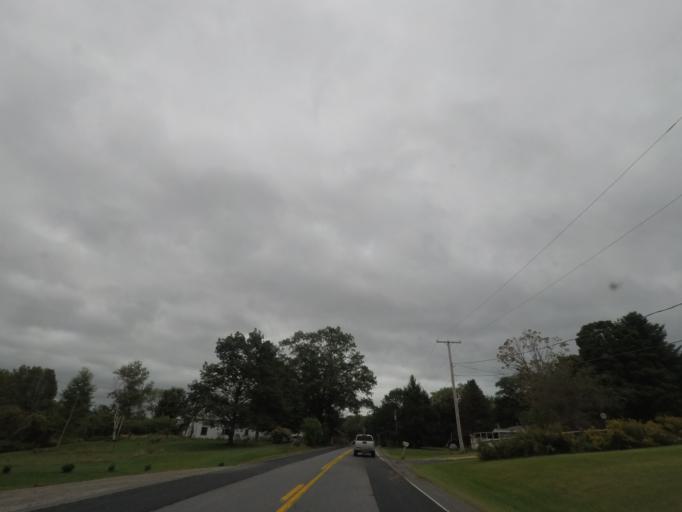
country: US
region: New York
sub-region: Rensselaer County
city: Hoosick Falls
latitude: 42.9511
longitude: -73.4074
